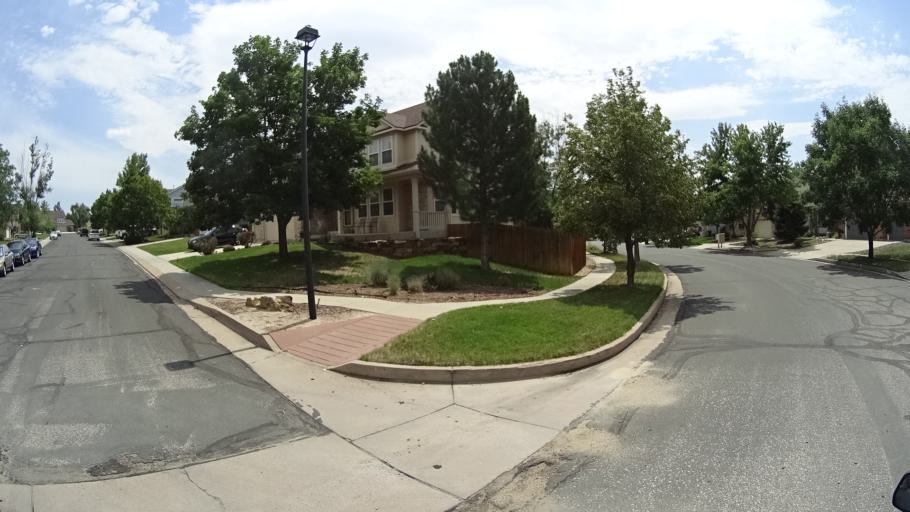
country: US
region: Colorado
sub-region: El Paso County
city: Air Force Academy
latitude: 38.9646
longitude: -104.7808
